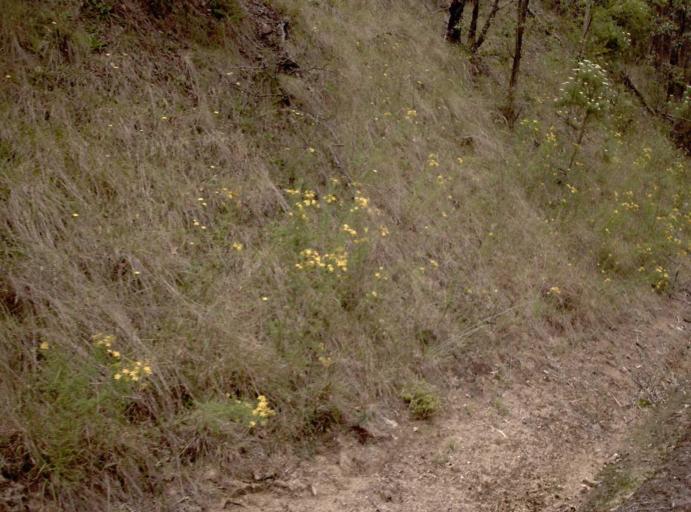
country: AU
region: New South Wales
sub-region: Bombala
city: Bombala
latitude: -37.3557
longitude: 149.2029
